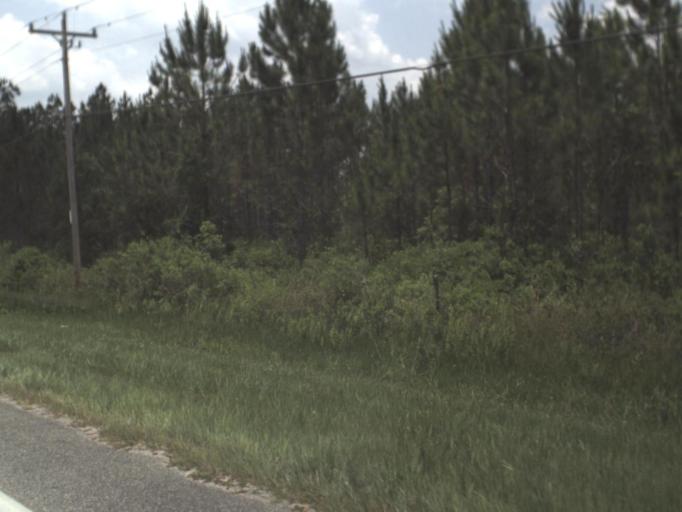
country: US
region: Florida
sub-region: Putnam County
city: Palatka
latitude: 29.5866
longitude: -81.7161
